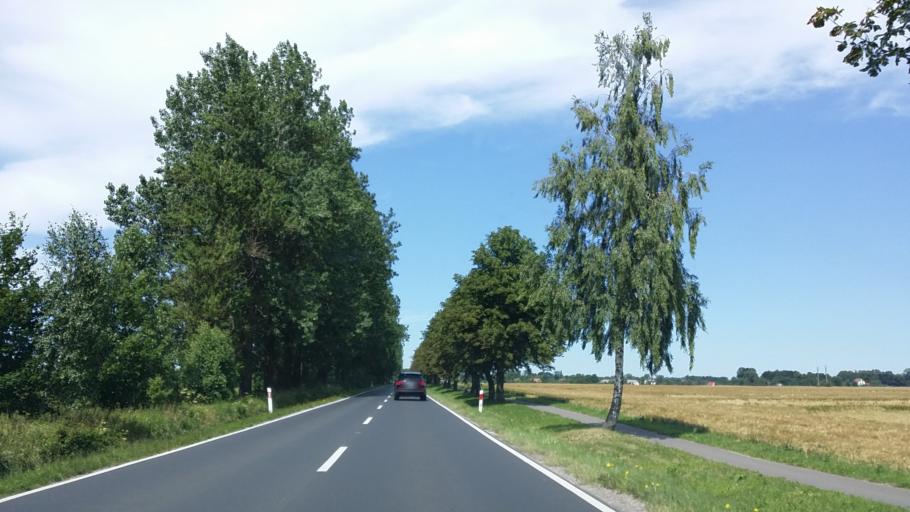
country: PL
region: West Pomeranian Voivodeship
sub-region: Powiat koszalinski
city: Mielno
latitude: 54.2305
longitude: 16.0746
